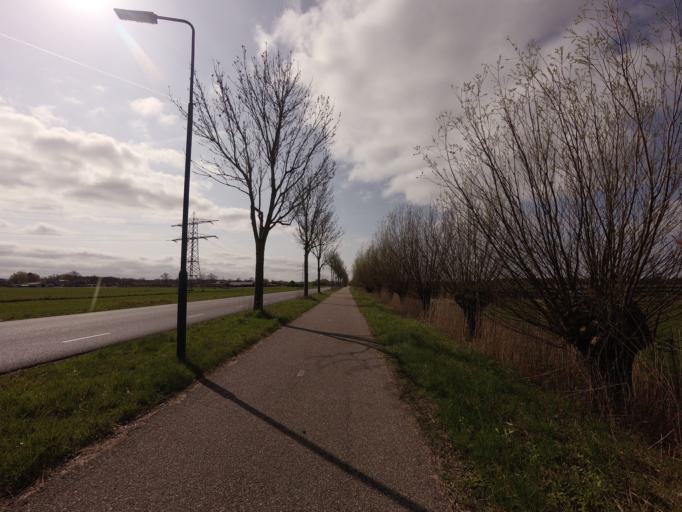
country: NL
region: Utrecht
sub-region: Gemeente Utrecht
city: Utrecht
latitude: 52.1435
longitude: 5.1180
